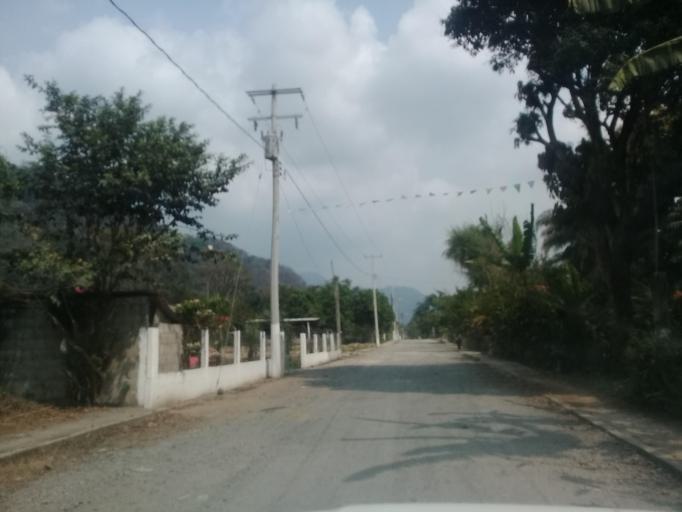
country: MX
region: Veracruz
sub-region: Ixtaczoquitlan
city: Capoluca
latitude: 18.8158
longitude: -96.9927
